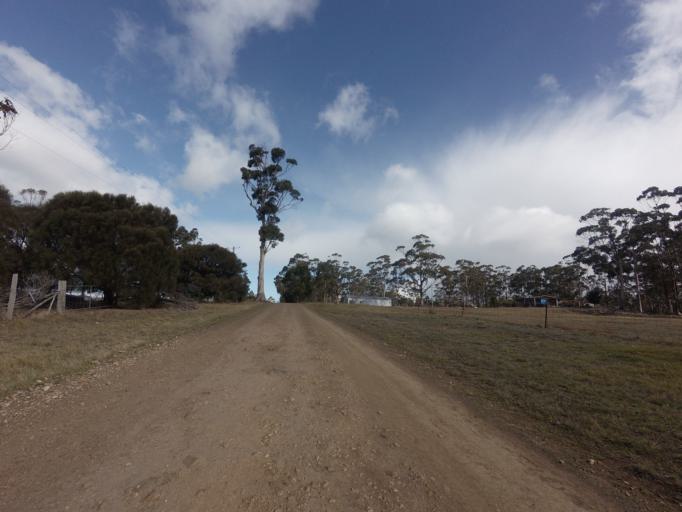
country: AU
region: Tasmania
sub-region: Sorell
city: Sorell
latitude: -42.3286
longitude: 147.9679
